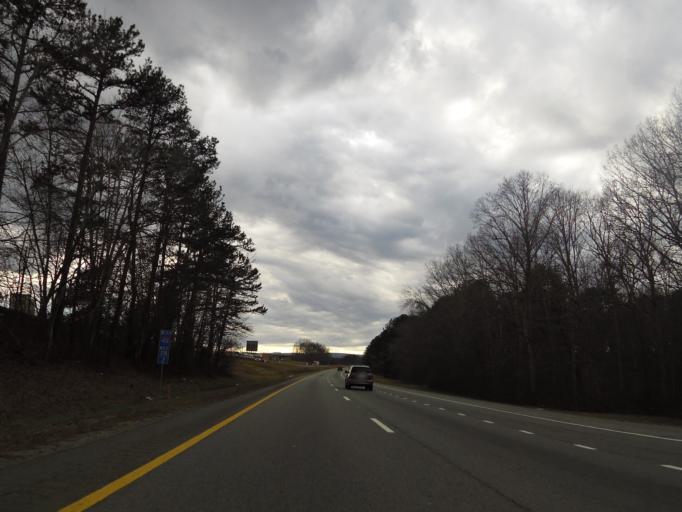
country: US
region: Tennessee
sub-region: Roane County
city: Rockwood
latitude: 35.8931
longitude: -84.7371
